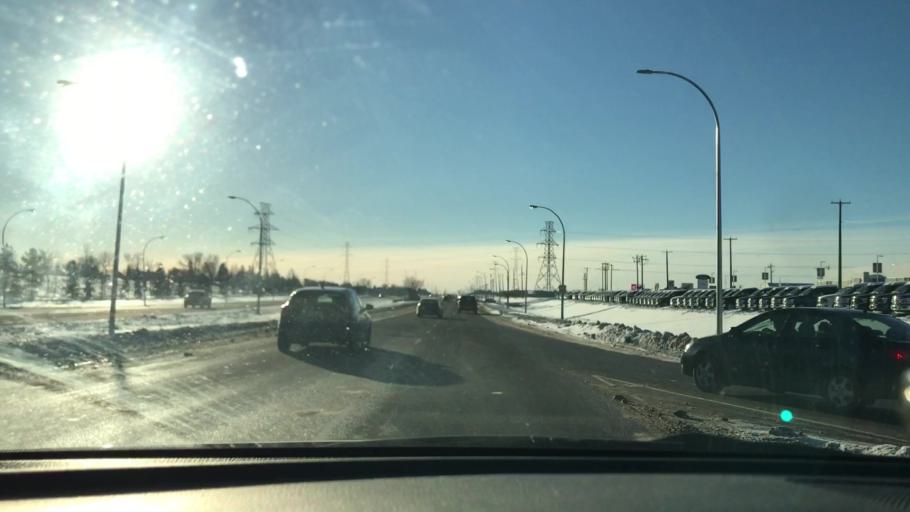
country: CA
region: Alberta
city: Edmonton
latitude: 53.4651
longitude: -113.4668
